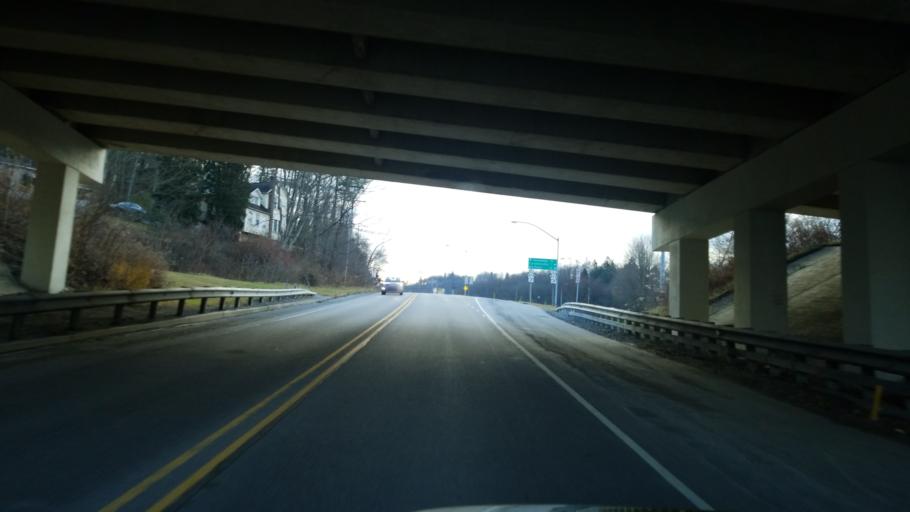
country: US
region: Pennsylvania
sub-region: Clearfield County
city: Clearfield
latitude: 41.0100
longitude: -78.4334
